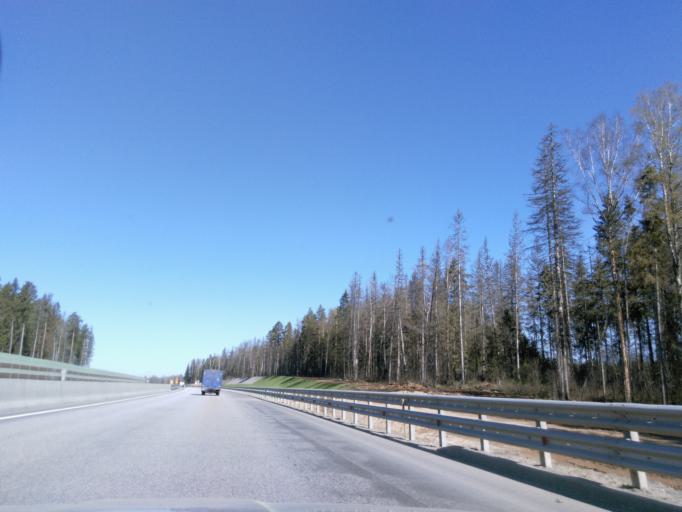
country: RU
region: Moskovskaya
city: Radumlya
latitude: 56.0920
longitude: 37.1967
